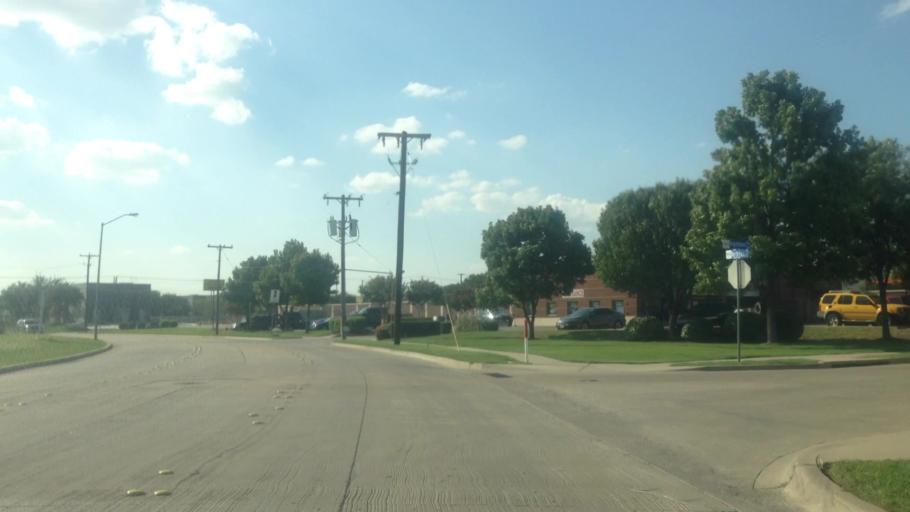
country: US
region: Texas
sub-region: Tarrant County
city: Watauga
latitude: 32.8863
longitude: -97.2577
